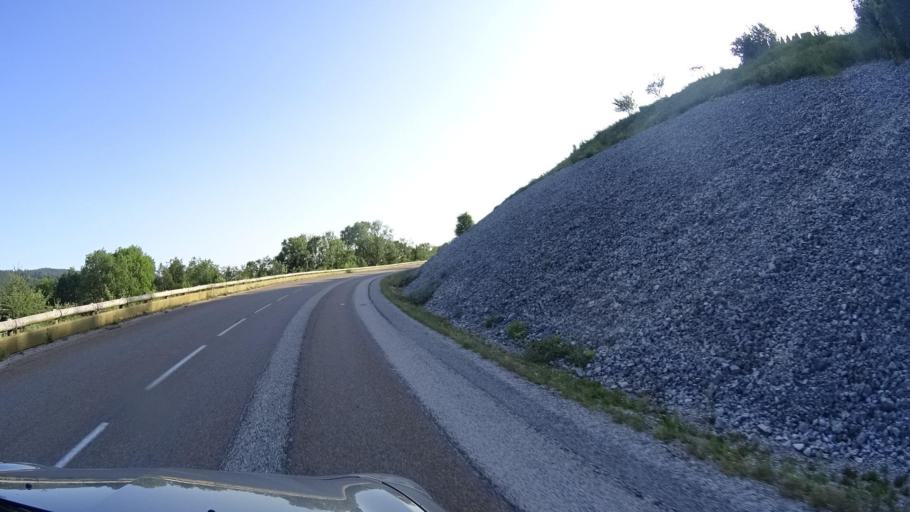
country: FR
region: Franche-Comte
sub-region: Departement du Jura
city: Morbier
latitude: 46.5287
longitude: 5.9885
